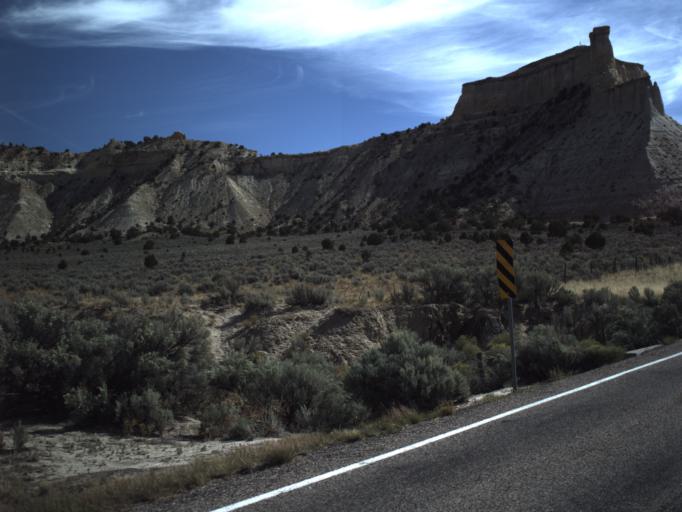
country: US
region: Utah
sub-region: Garfield County
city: Panguitch
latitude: 37.5607
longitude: -112.0264
